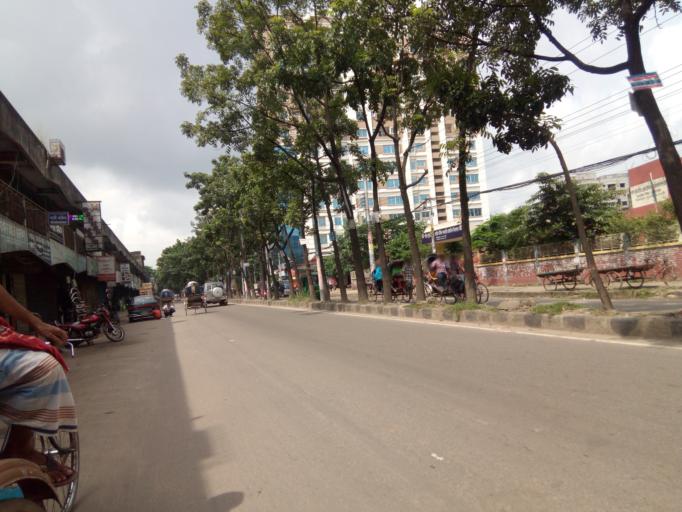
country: BD
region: Dhaka
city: Azimpur
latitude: 23.7358
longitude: 90.3890
